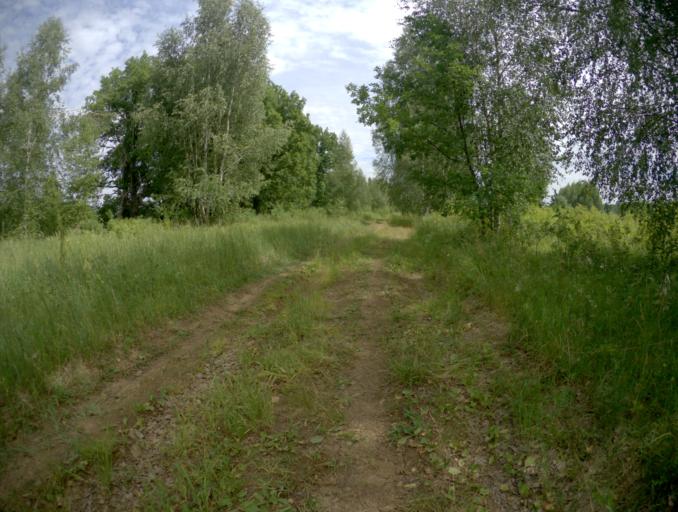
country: RU
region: Vladimir
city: Raduzhnyy
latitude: 56.0307
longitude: 40.2548
